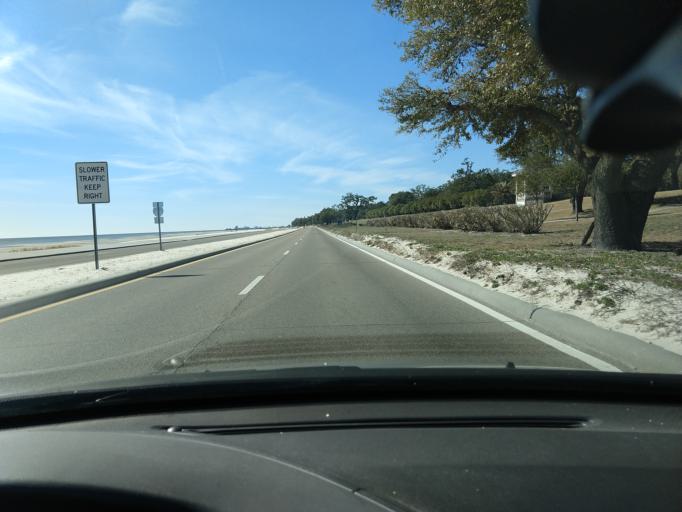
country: US
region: Mississippi
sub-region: Harrison County
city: Pass Christian
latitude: 30.3240
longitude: -89.2188
